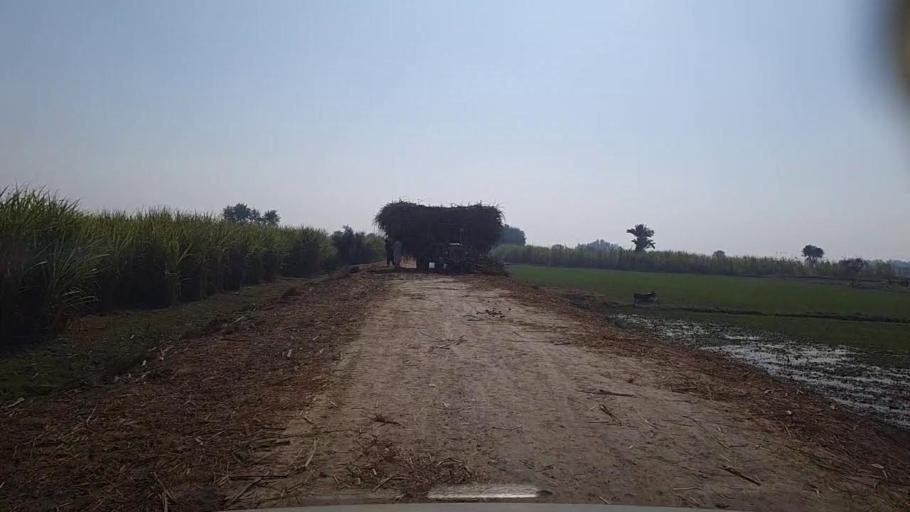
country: PK
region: Sindh
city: Mirpur Mathelo
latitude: 28.0683
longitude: 69.6172
